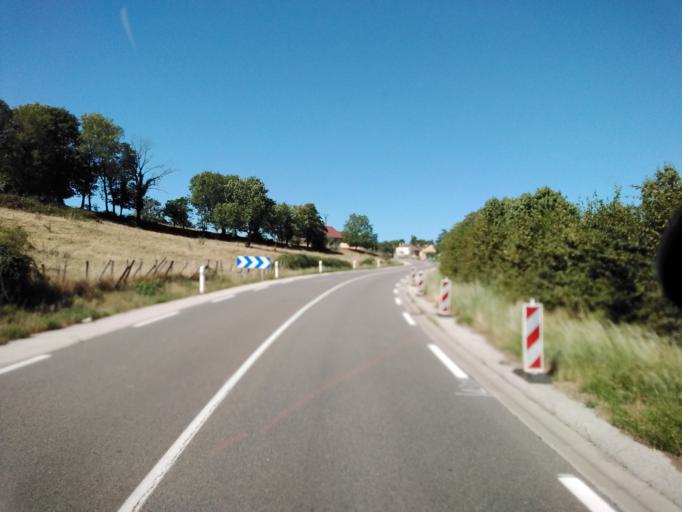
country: FR
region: Franche-Comte
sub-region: Departement du Jura
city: Poligny
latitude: 46.8648
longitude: 5.7148
